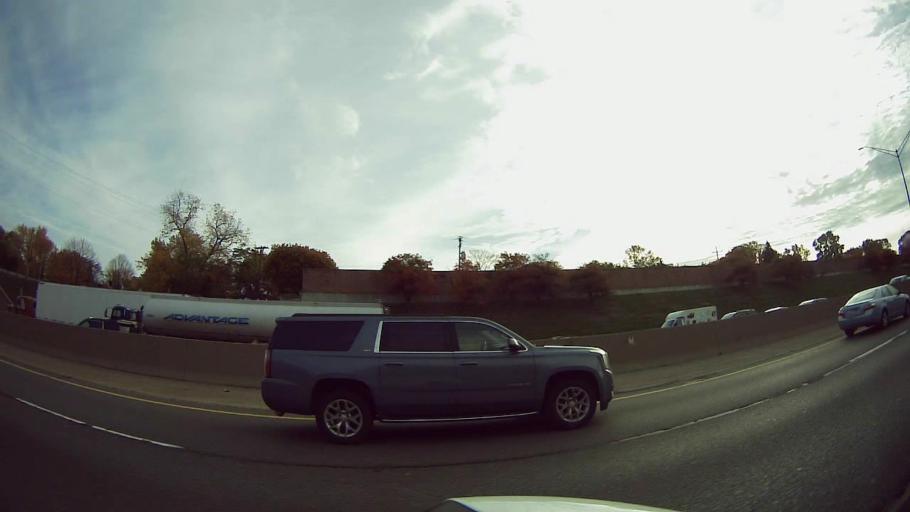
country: US
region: Michigan
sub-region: Oakland County
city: Madison Heights
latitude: 42.4826
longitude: -83.1138
